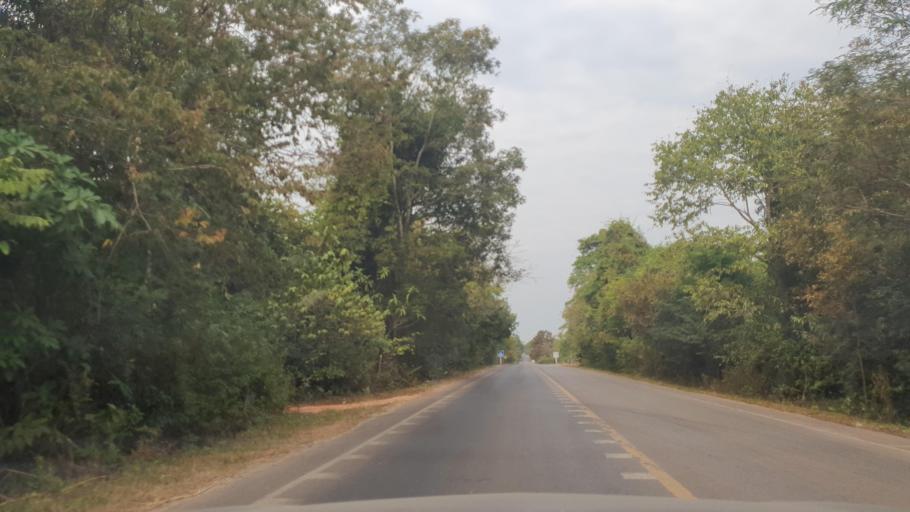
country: TH
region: Changwat Bueng Kan
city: Bung Khla
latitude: 18.2381
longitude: 104.0245
